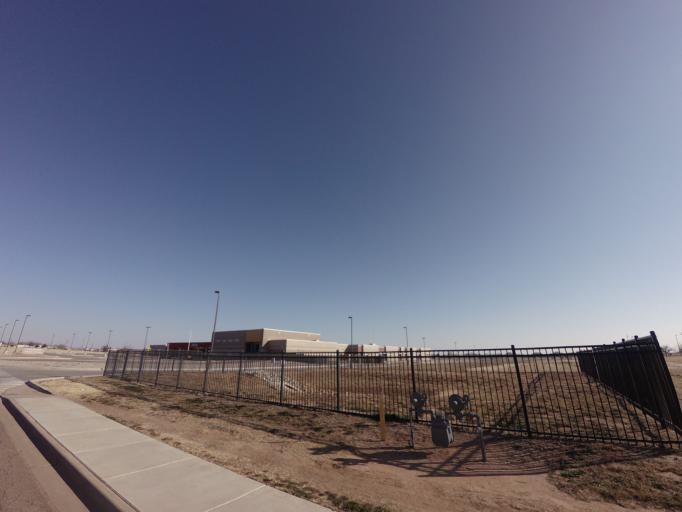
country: US
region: New Mexico
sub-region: Curry County
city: Clovis
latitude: 34.3849
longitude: -103.1938
